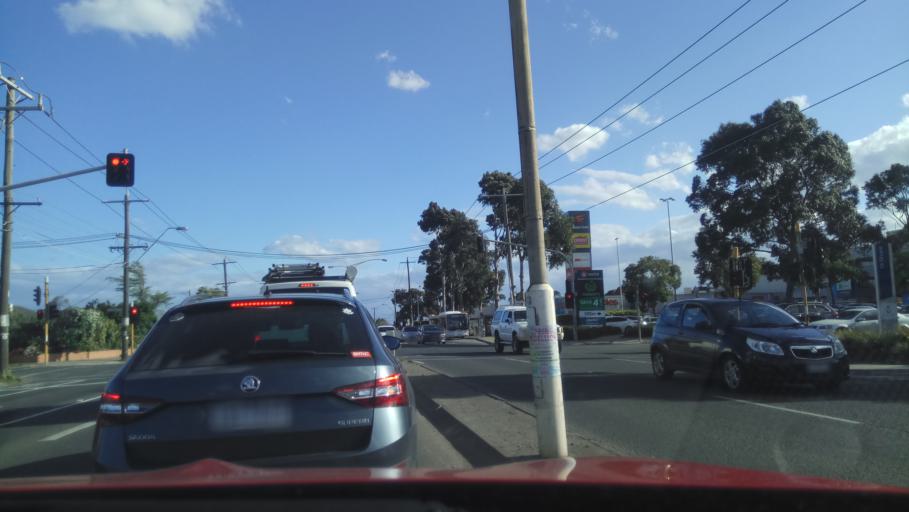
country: AU
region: Victoria
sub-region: Hobsons Bay
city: Altona North
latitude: -37.8268
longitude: 144.8490
